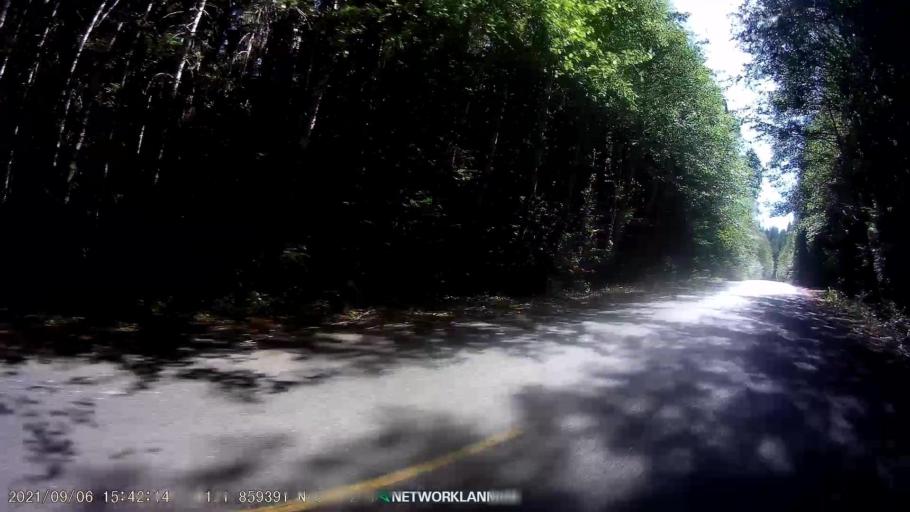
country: US
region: Washington
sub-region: Skamania County
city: Carson
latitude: 46.1726
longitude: -121.8597
